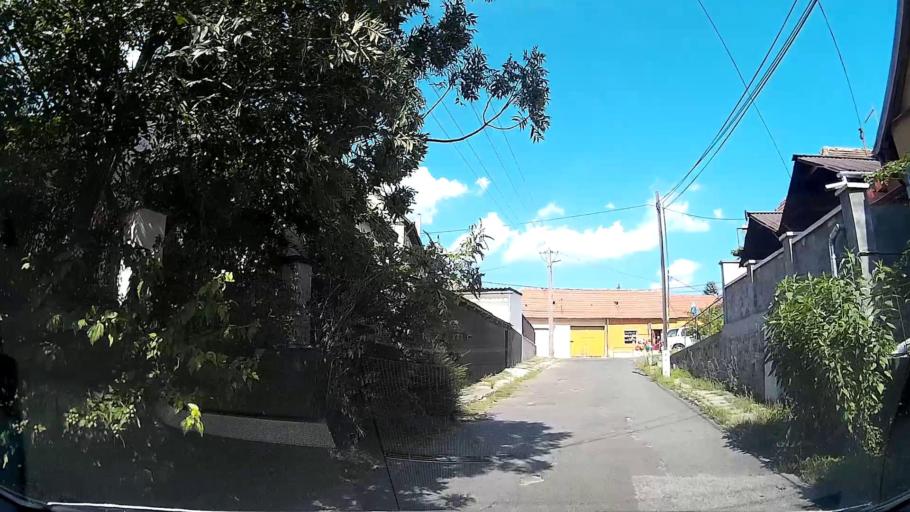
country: HU
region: Pest
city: Tahitotfalu
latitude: 47.7539
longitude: 19.0893
